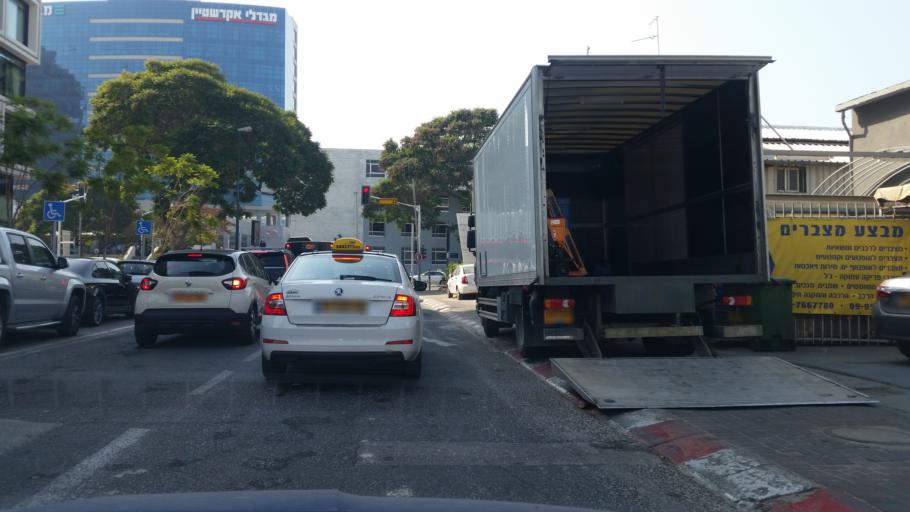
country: IL
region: Tel Aviv
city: Herzliya Pituah
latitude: 32.1629
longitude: 34.8081
